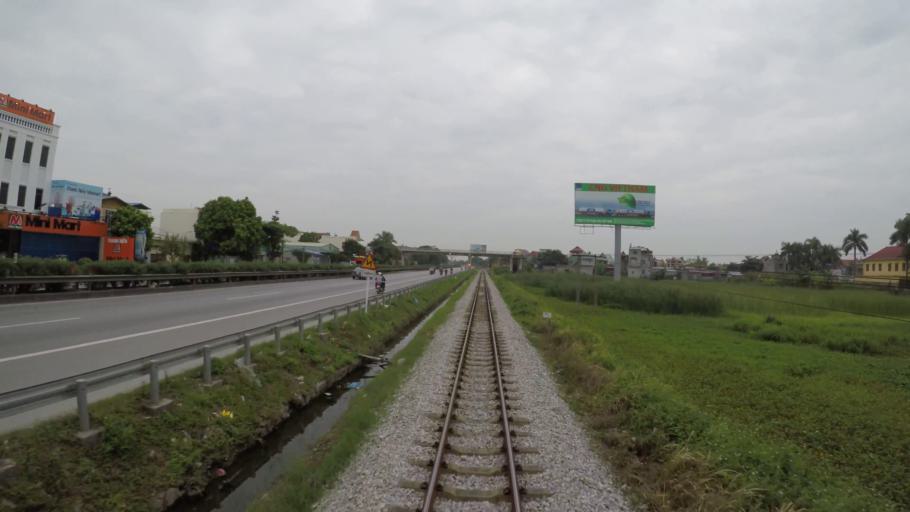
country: VN
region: Hai Duong
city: Phu Thai
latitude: 20.9227
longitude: 106.5590
